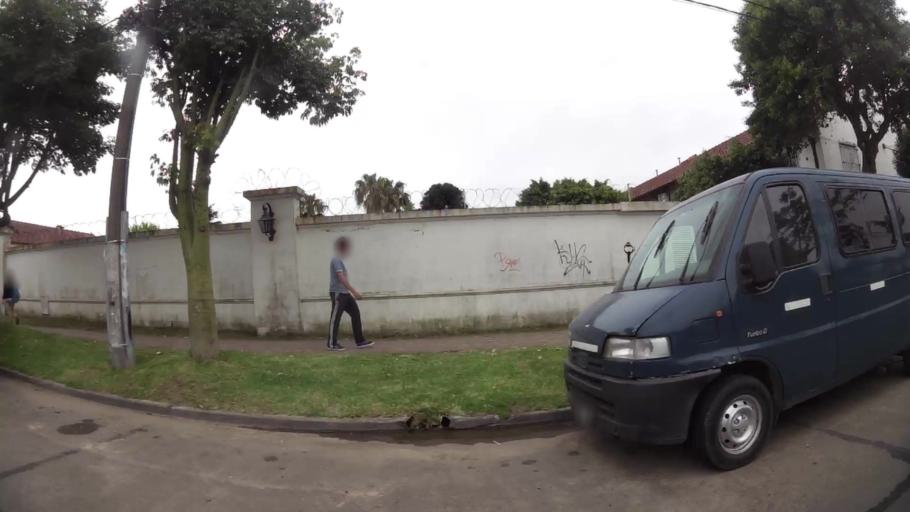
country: AR
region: Buenos Aires
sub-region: Partido de Campana
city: Campana
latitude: -34.1758
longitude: -58.9563
